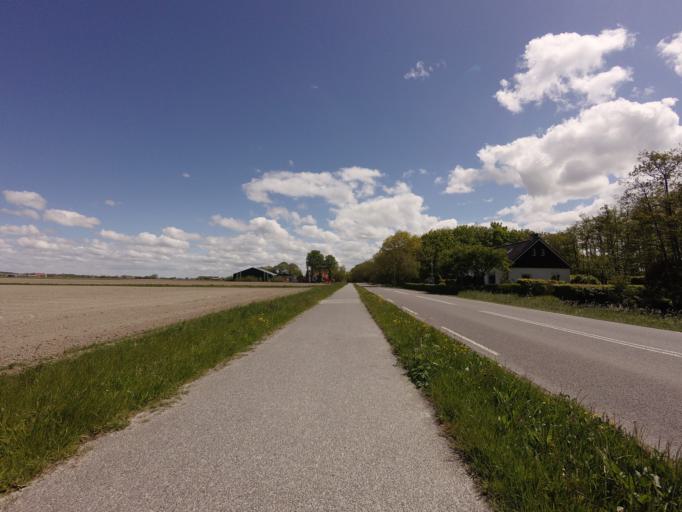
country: NL
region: Friesland
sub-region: Gemeente Harlingen
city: Harlingen
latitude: 53.1376
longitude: 5.4518
